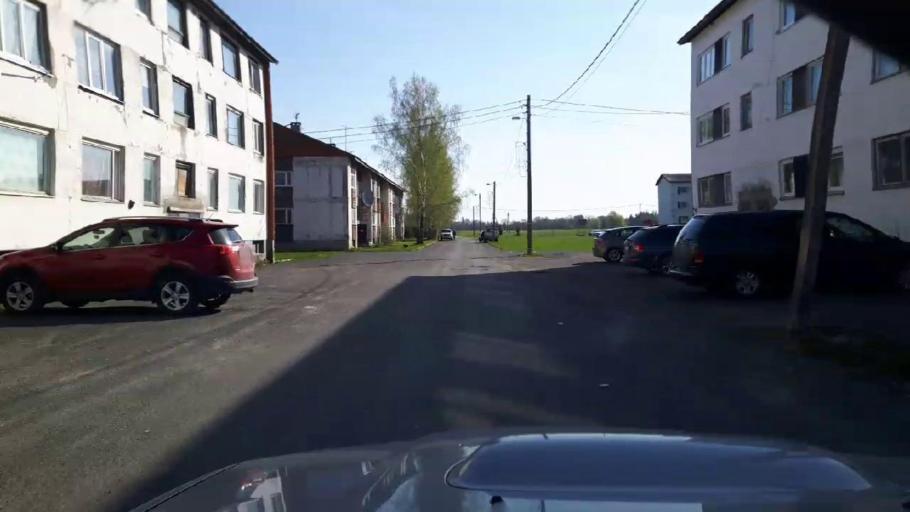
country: EE
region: Paernumaa
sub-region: Tootsi vald
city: Tootsi
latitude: 58.4946
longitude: 24.9053
